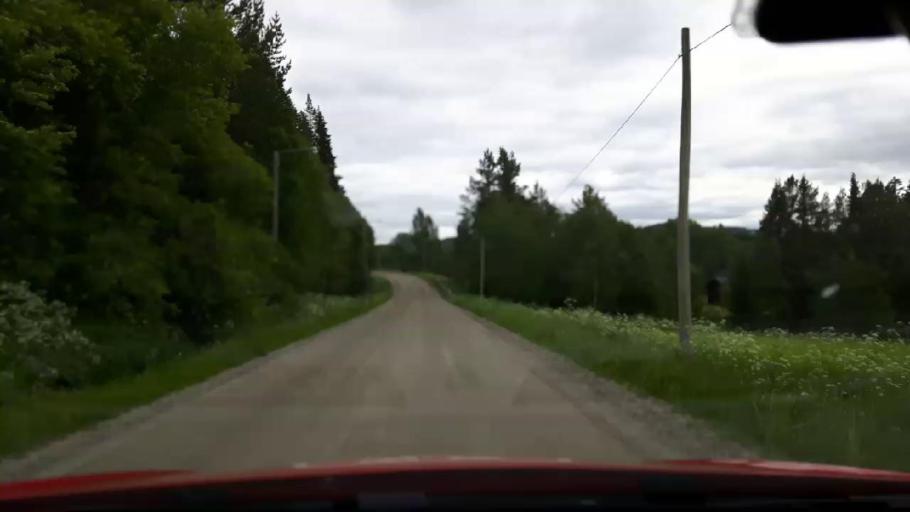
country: SE
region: Jaemtland
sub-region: Ragunda Kommun
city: Hammarstrand
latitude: 63.1701
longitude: 16.2048
